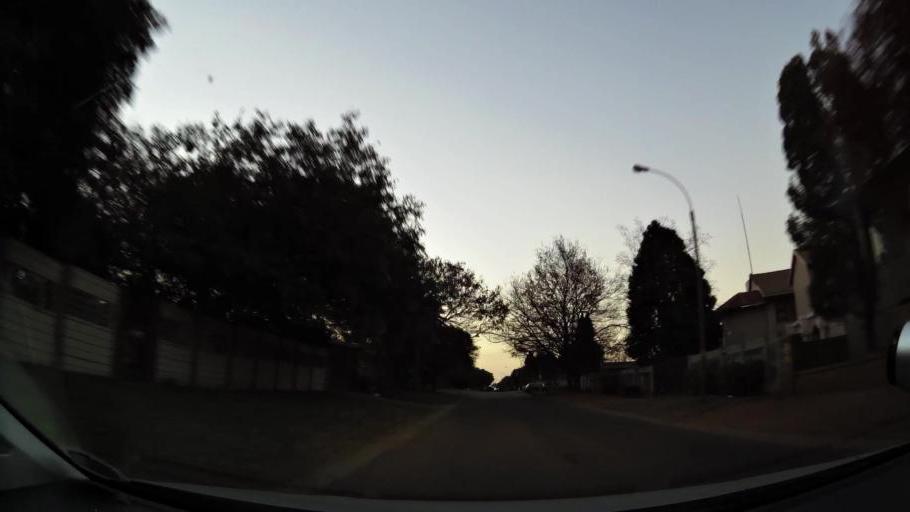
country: ZA
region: Gauteng
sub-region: Ekurhuleni Metropolitan Municipality
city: Tembisa
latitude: -26.0522
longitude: 28.2459
